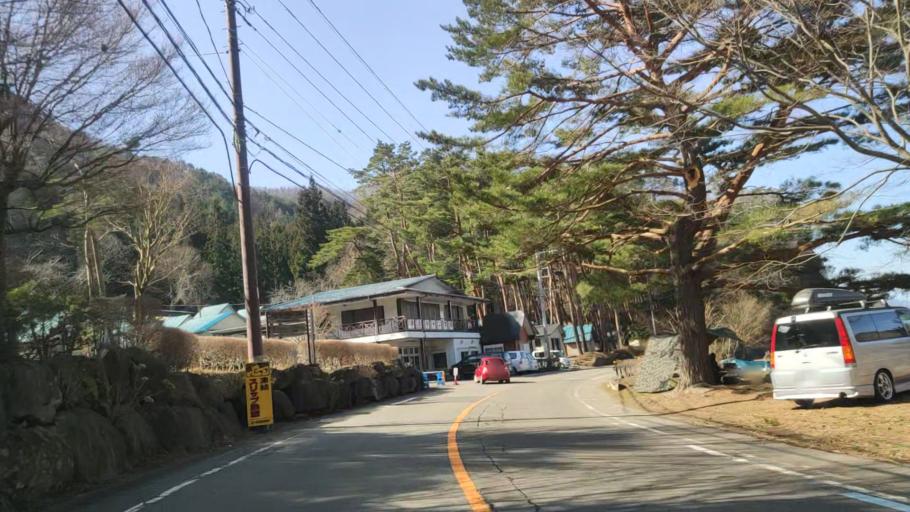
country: JP
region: Yamanashi
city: Fujikawaguchiko
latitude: 35.4994
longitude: 138.6992
